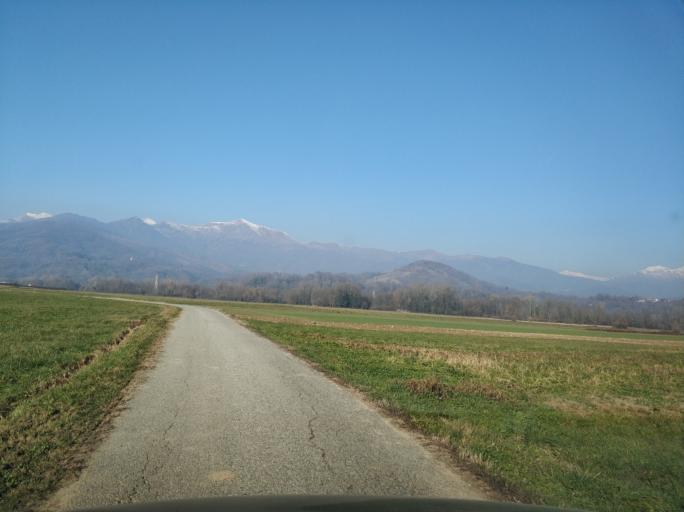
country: IT
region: Piedmont
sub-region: Provincia di Torino
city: Levone
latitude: 45.3103
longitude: 7.6241
